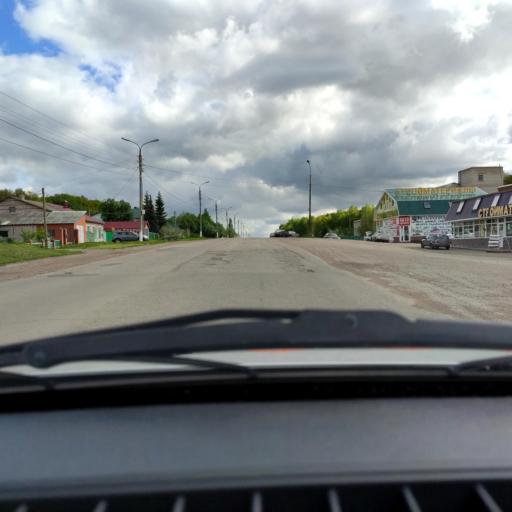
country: RU
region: Bashkortostan
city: Tolbazy
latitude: 54.0154
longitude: 55.8972
